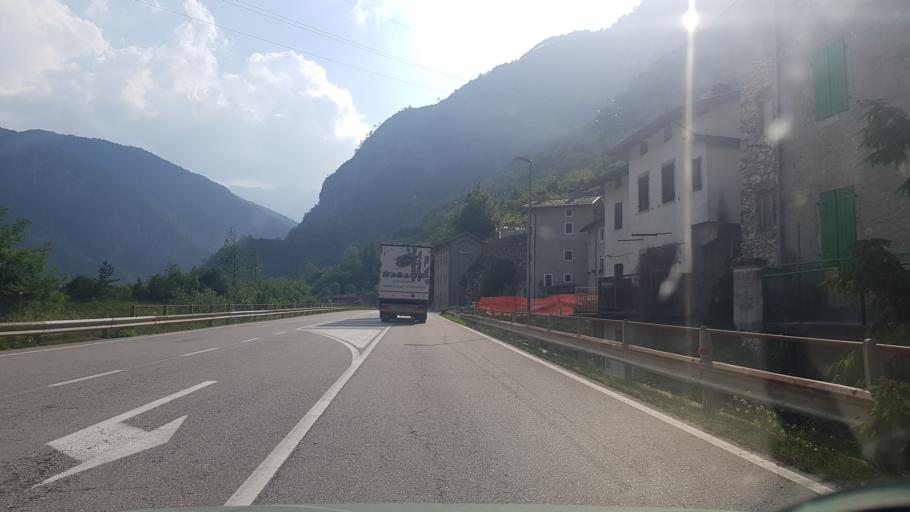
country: IT
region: Friuli Venezia Giulia
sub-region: Provincia di Udine
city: Chiusaforte
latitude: 46.4047
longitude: 13.2931
